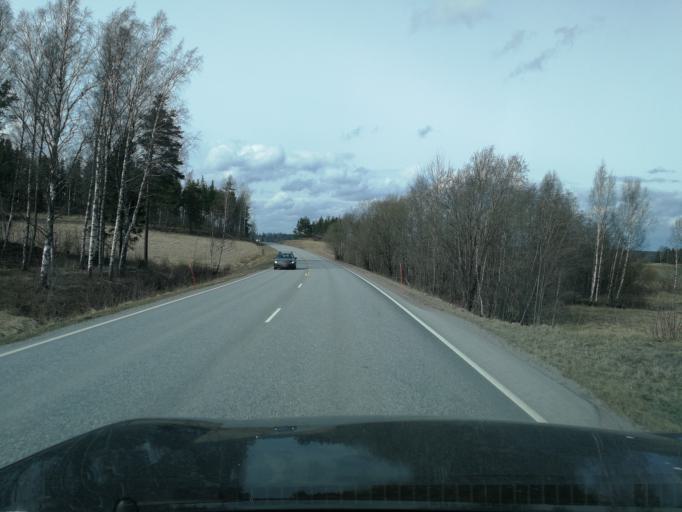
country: FI
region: Uusimaa
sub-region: Helsinki
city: Siuntio
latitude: 60.1069
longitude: 24.2464
